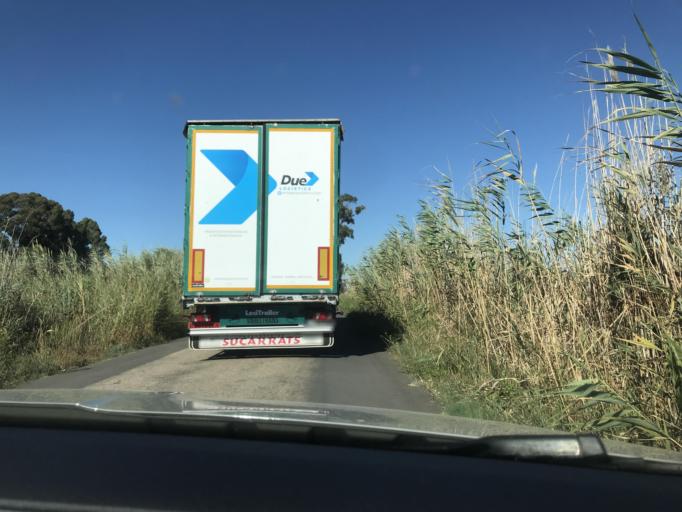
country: ES
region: Catalonia
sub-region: Provincia de Tarragona
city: Deltebre
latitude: 40.6582
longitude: 0.7740
